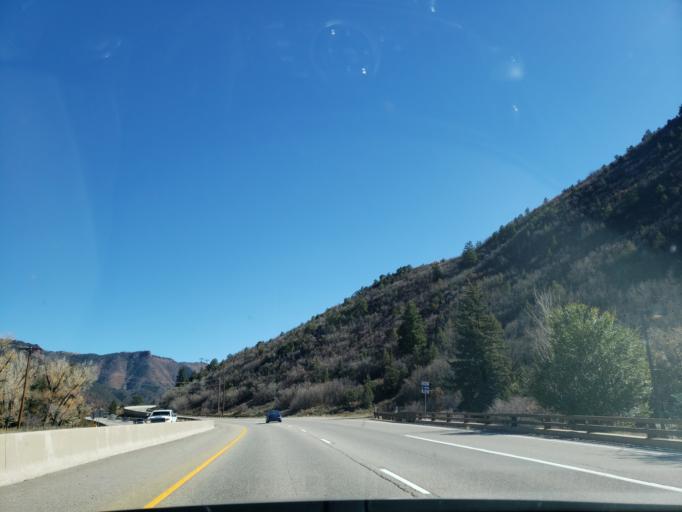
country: US
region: Colorado
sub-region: Eagle County
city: Basalt
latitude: 39.3306
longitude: -106.9831
